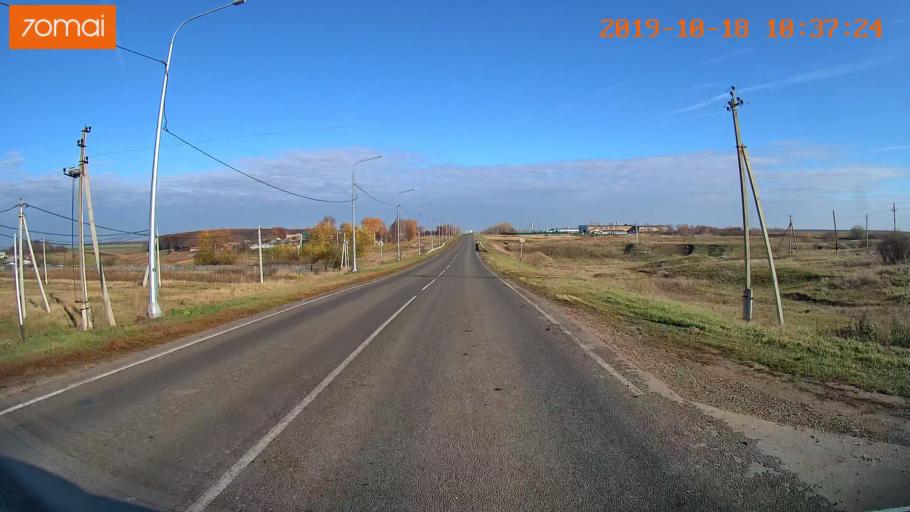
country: RU
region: Tula
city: Kurkino
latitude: 53.5614
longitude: 38.6319
